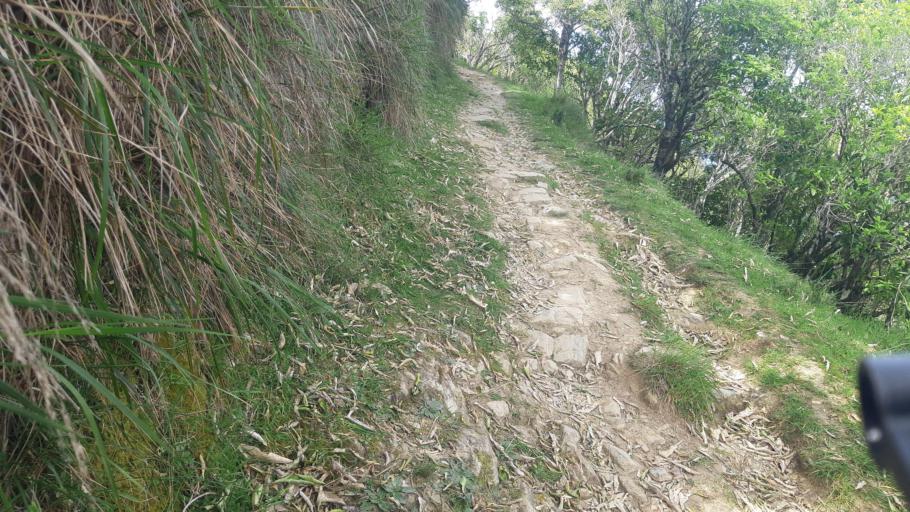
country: NZ
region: Marlborough
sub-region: Marlborough District
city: Picton
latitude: -41.2502
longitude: 173.9606
